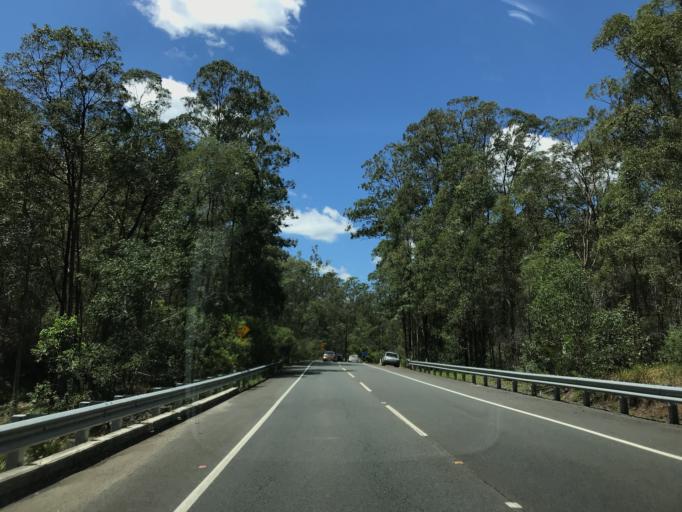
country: AU
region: Queensland
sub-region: Brisbane
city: Kenmore Hills
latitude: -27.4767
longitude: 152.9264
